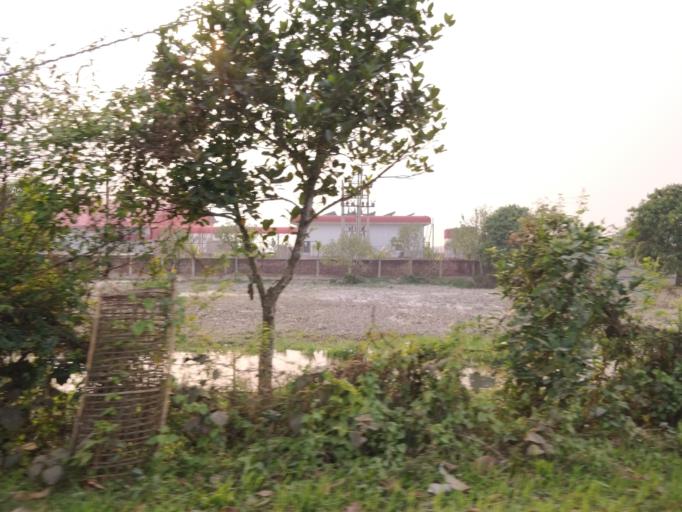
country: BD
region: Sylhet
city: Habiganj
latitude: 24.1358
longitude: 91.3517
